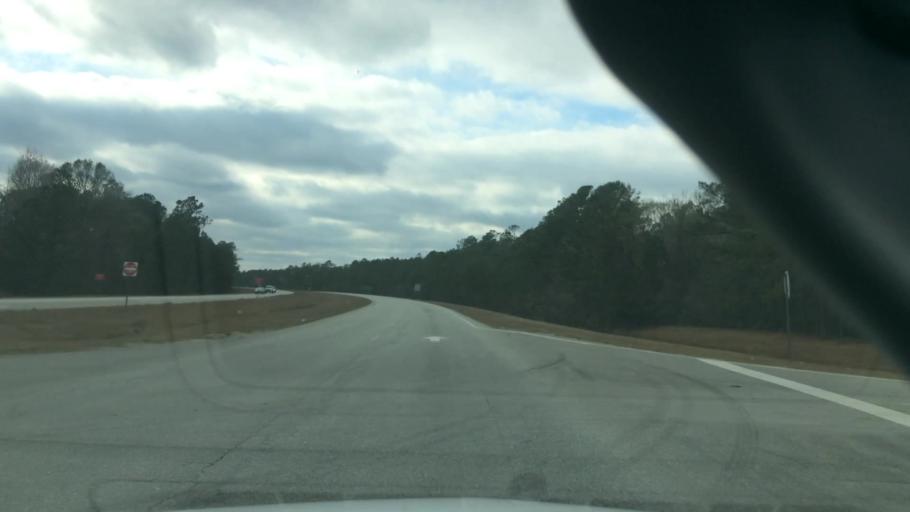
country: US
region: North Carolina
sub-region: Brunswick County
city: Bolivia
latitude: 34.0630
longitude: -78.1992
